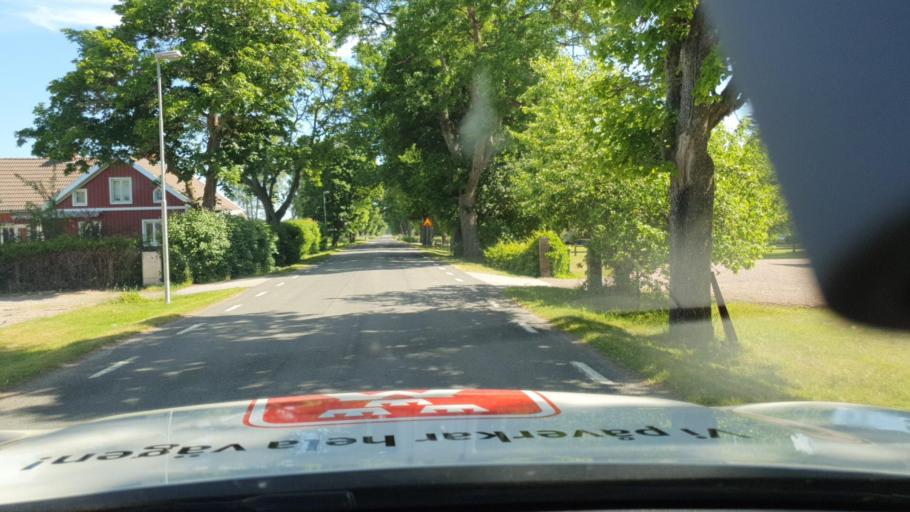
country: SE
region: Vaestra Goetaland
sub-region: Tidaholms Kommun
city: Olofstorp
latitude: 58.2718
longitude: 13.9120
